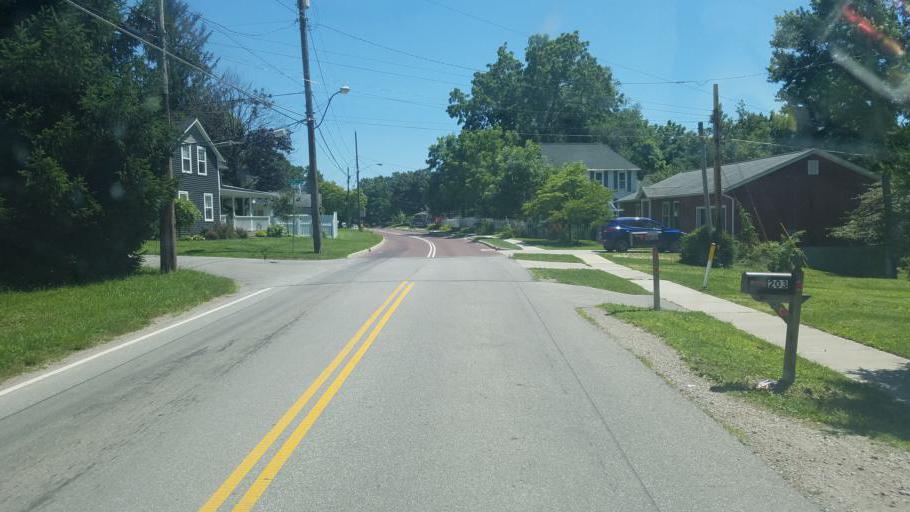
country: US
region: Ohio
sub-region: Delaware County
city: Sunbury
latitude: 40.2193
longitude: -82.8812
